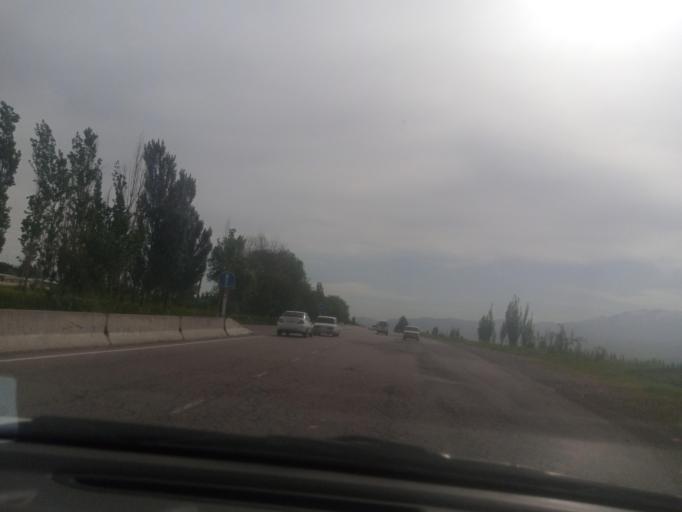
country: UZ
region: Toshkent
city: Angren
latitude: 40.9652
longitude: 69.9571
